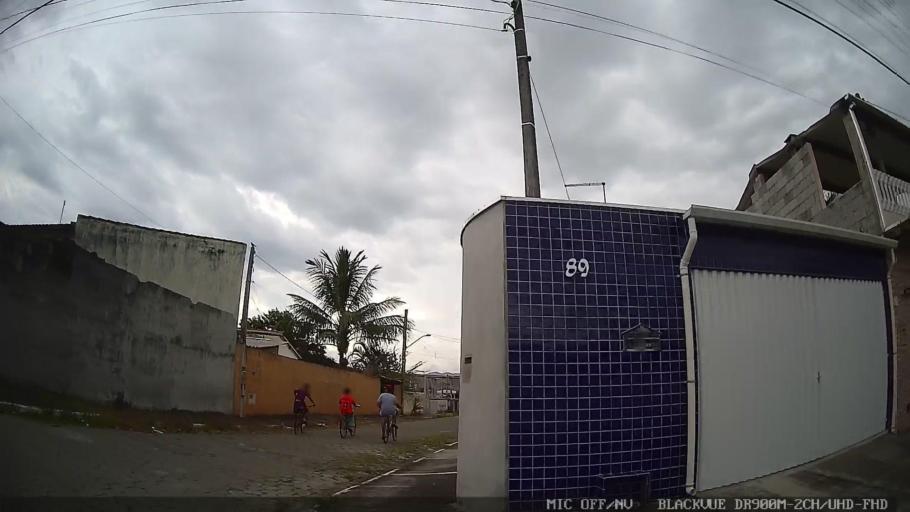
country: BR
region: Sao Paulo
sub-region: Caraguatatuba
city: Caraguatatuba
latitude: -23.6816
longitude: -45.4530
